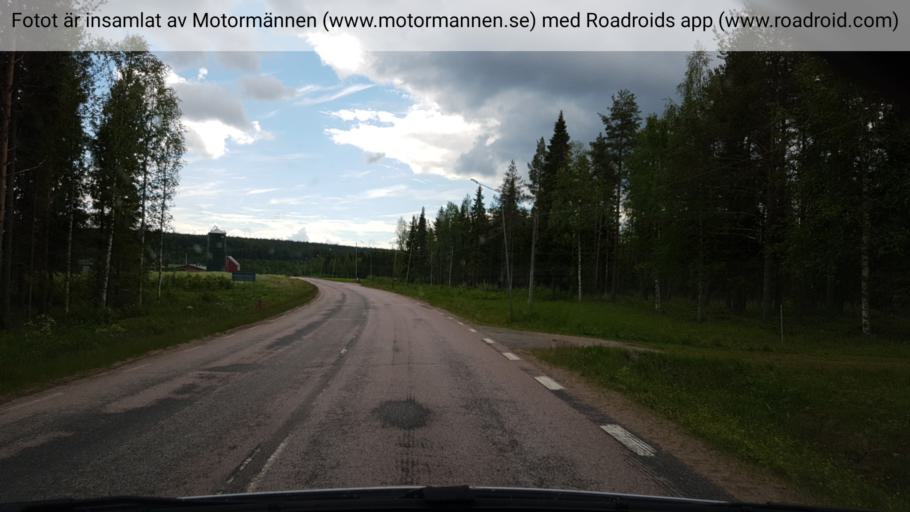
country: FI
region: Lapland
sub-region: Torniolaakso
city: Ylitornio
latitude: 66.1896
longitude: 23.7137
